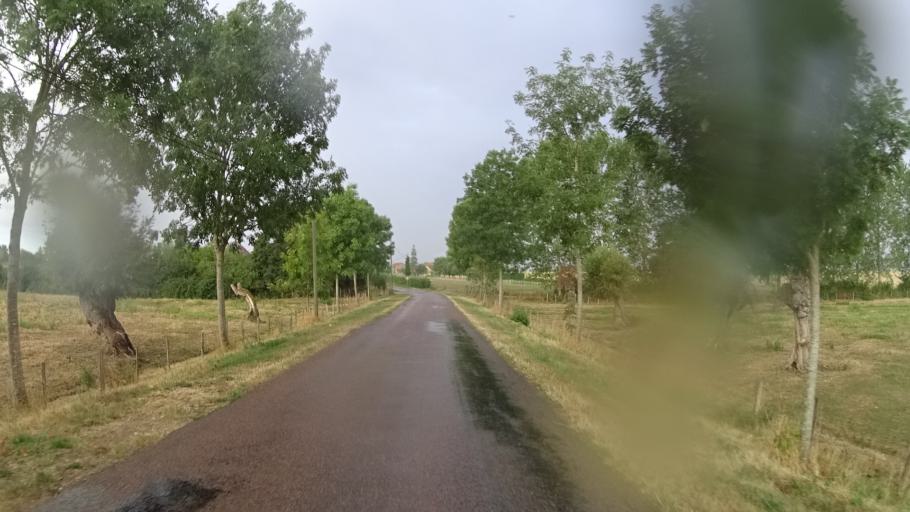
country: FR
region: Bourgogne
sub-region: Departement de Saone-et-Loire
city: Verdun-sur-le-Doubs
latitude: 46.9610
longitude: 5.0183
